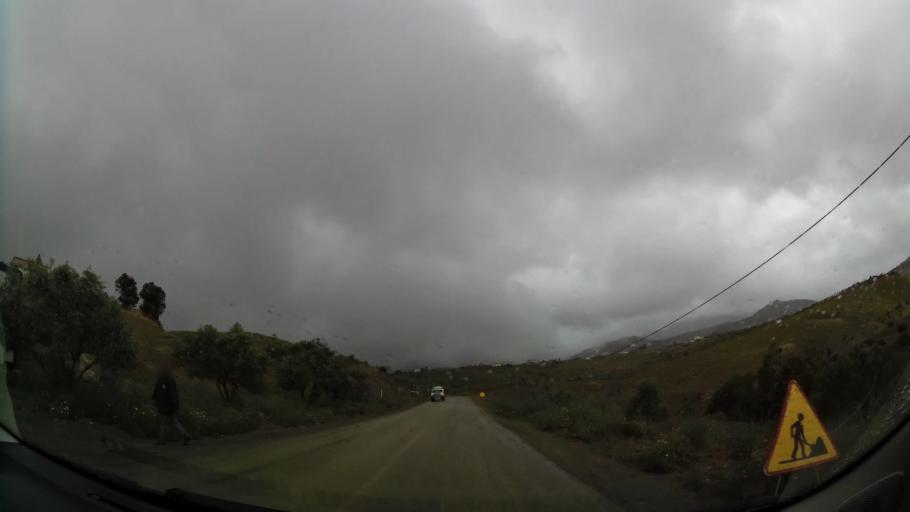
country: MA
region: Oriental
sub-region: Nador
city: Midar
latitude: 34.8906
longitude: -3.7585
